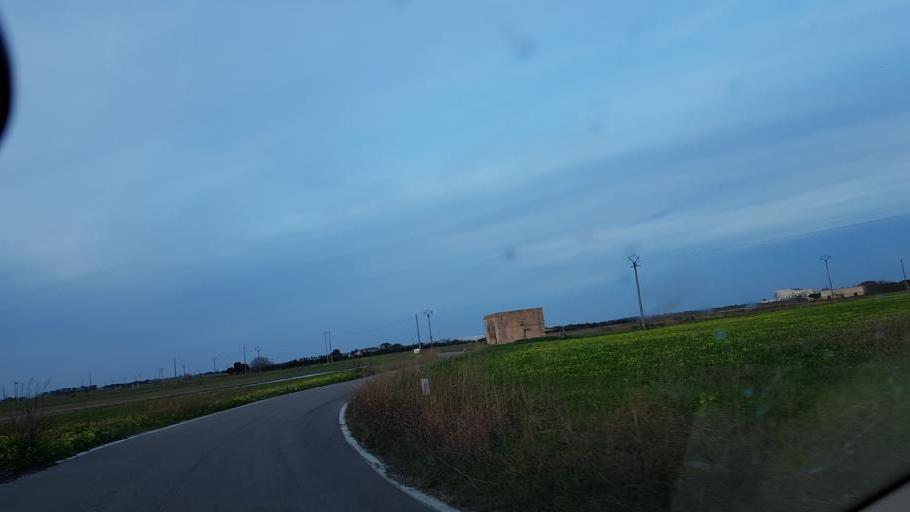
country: IT
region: Apulia
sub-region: Provincia di Brindisi
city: Brindisi
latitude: 40.6601
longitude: 17.9109
